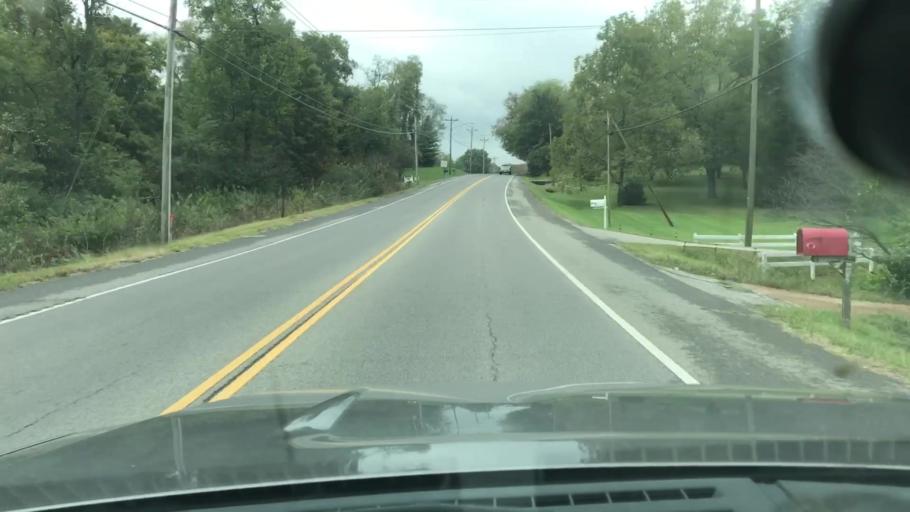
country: US
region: Tennessee
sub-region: Williamson County
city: Franklin
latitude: 35.9622
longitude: -86.8400
